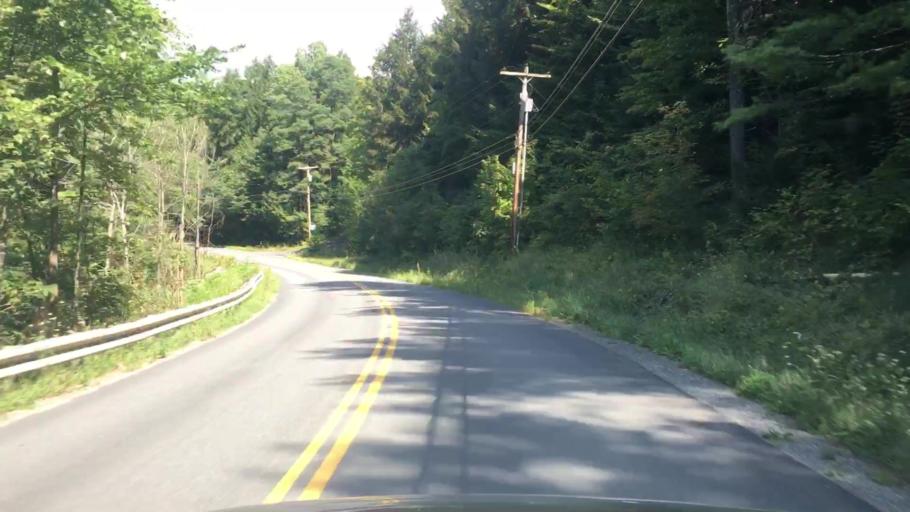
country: US
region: Vermont
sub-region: Windham County
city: West Brattleboro
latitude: 42.8010
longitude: -72.6191
